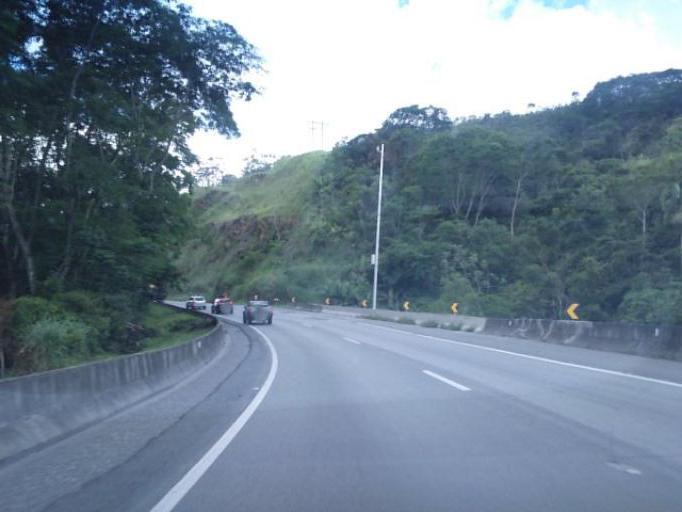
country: BR
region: Sao Paulo
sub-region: Cajati
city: Cajati
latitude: -24.7969
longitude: -48.2088
